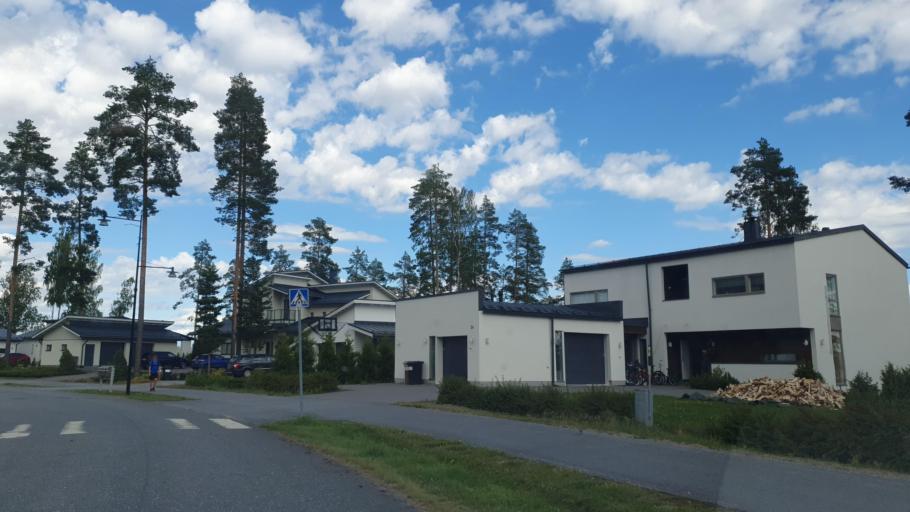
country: FI
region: Central Finland
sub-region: Jyvaeskylae
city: Saeynaetsalo
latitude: 62.1617
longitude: 25.7685
